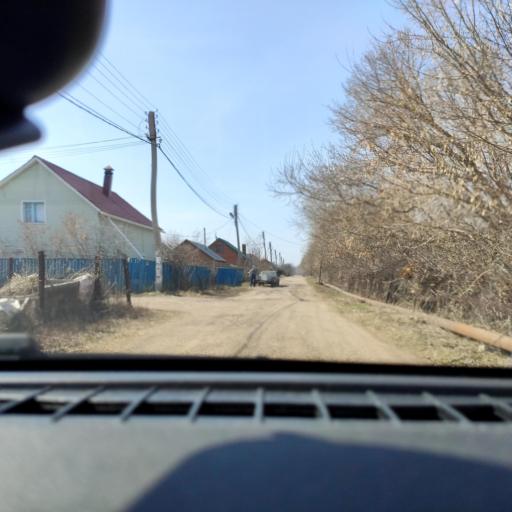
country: RU
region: Samara
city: Podstepki
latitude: 53.5202
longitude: 49.1069
